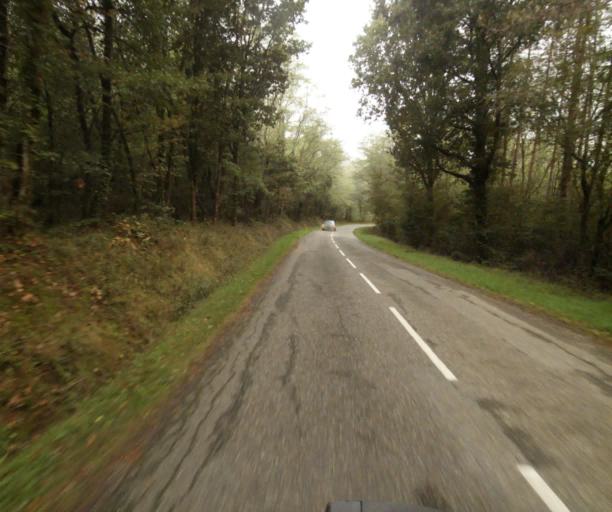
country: FR
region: Midi-Pyrenees
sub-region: Departement du Tarn-et-Garonne
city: Saint-Nauphary
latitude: 43.9364
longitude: 1.4620
